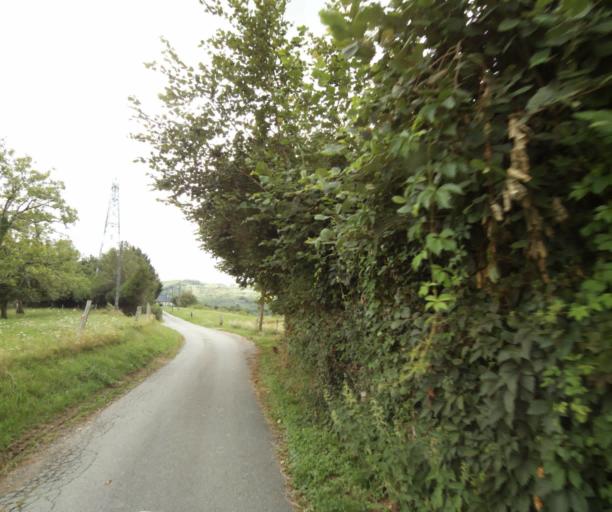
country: FR
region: Limousin
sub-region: Departement de la Correze
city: Sainte-Fortunade
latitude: 45.1762
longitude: 1.8364
